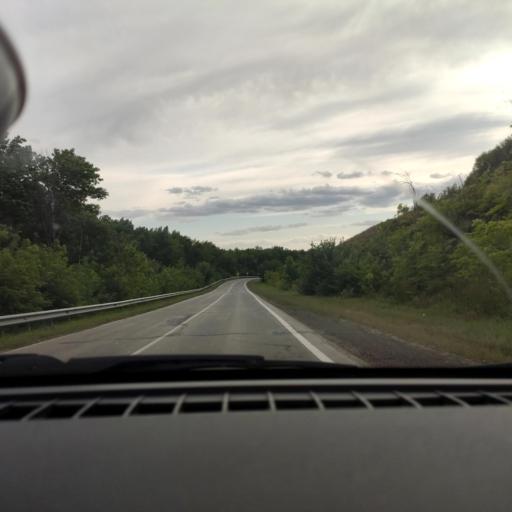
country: RU
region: Samara
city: Krasnyy Yar
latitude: 53.4392
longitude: 50.5882
